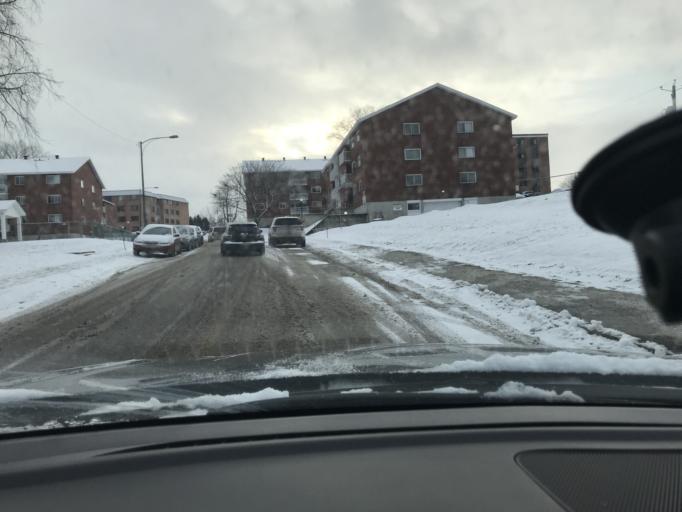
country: CA
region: Quebec
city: Quebec
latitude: 46.7891
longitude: -71.2767
